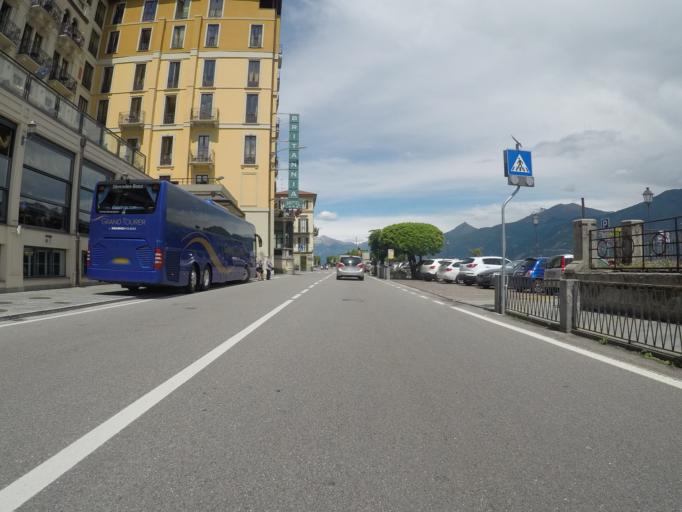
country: IT
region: Lombardy
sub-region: Provincia di Como
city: Cadenabbia
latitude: 45.9919
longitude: 9.2379
